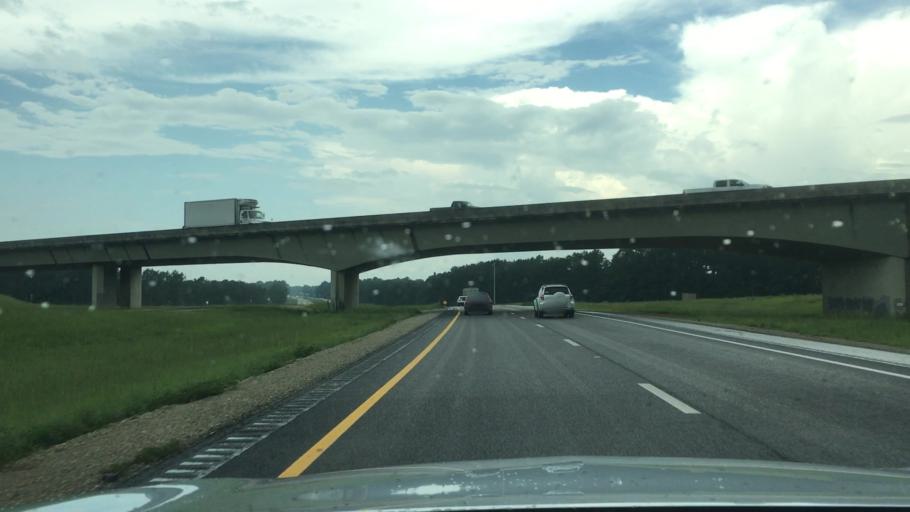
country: US
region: Mississippi
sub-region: Forrest County
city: Hattiesburg
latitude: 31.2388
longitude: -89.3233
